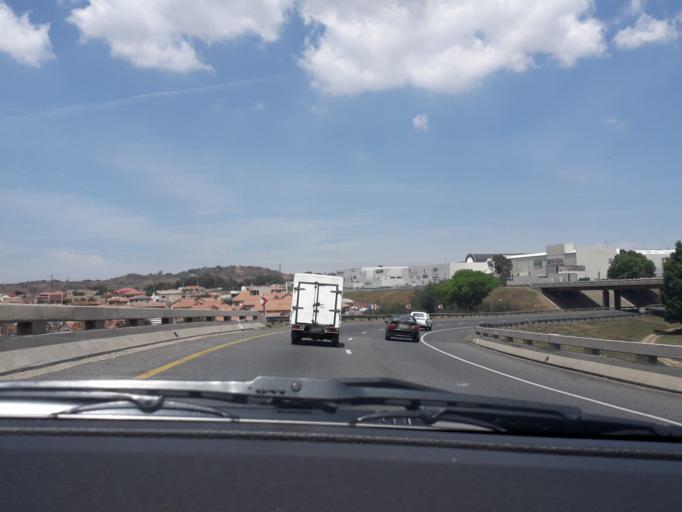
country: ZA
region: Gauteng
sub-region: City of Johannesburg Metropolitan Municipality
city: Johannesburg
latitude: -26.2628
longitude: 27.9864
